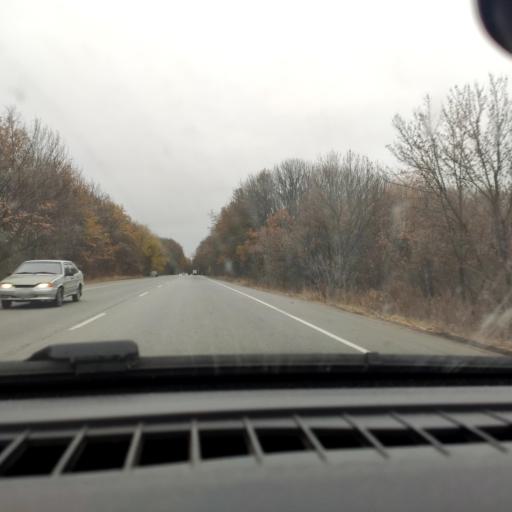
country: RU
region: Voronezj
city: Devitsa
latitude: 51.6286
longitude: 38.9906
